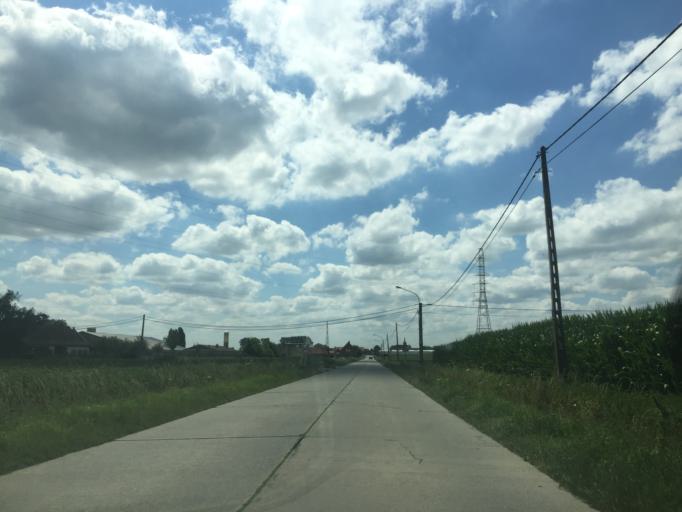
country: BE
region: Flanders
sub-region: Provincie West-Vlaanderen
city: Staden
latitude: 50.9548
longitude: 2.9890
